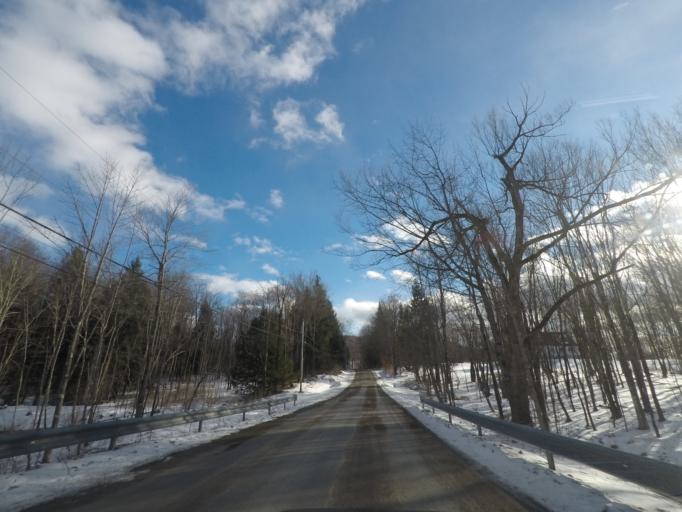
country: US
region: New York
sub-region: Rensselaer County
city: Poestenkill
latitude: 42.7563
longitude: -73.4885
